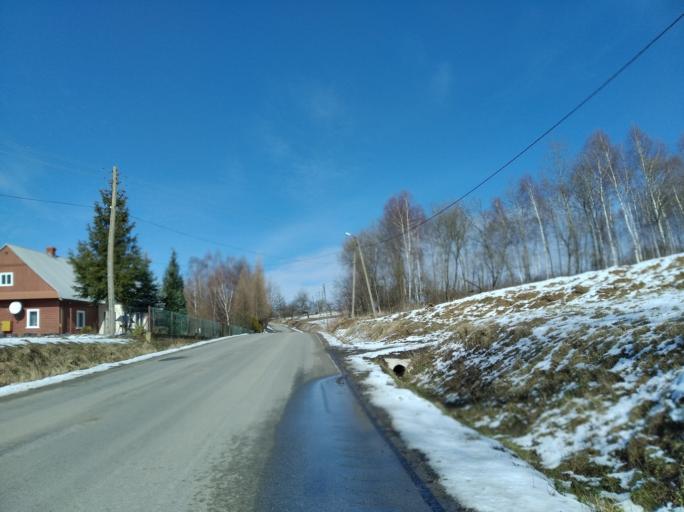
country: PL
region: Subcarpathian Voivodeship
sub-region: Powiat brzozowski
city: Jablonica Polska
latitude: 49.7213
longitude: 21.8798
